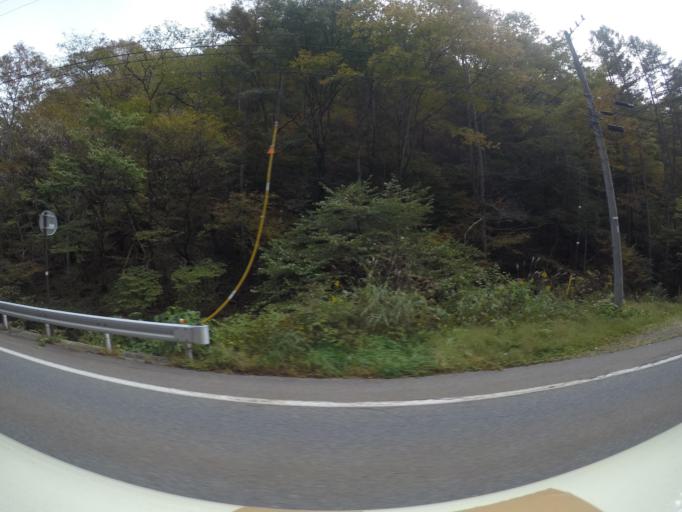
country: JP
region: Nagano
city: Ina
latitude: 35.9074
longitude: 137.7791
